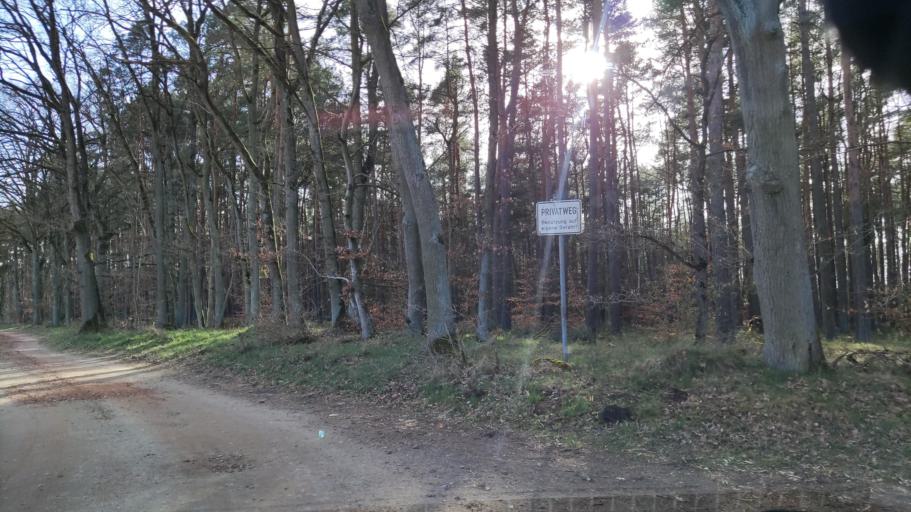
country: DE
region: Lower Saxony
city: Bienenbuttel
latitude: 53.1410
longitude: 10.4700
